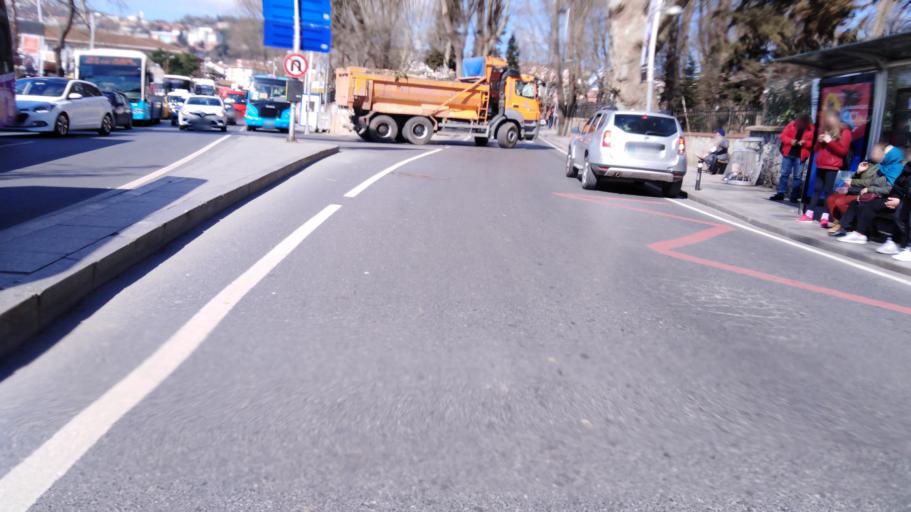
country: TR
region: Istanbul
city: Arikoey
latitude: 41.1712
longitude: 29.0537
